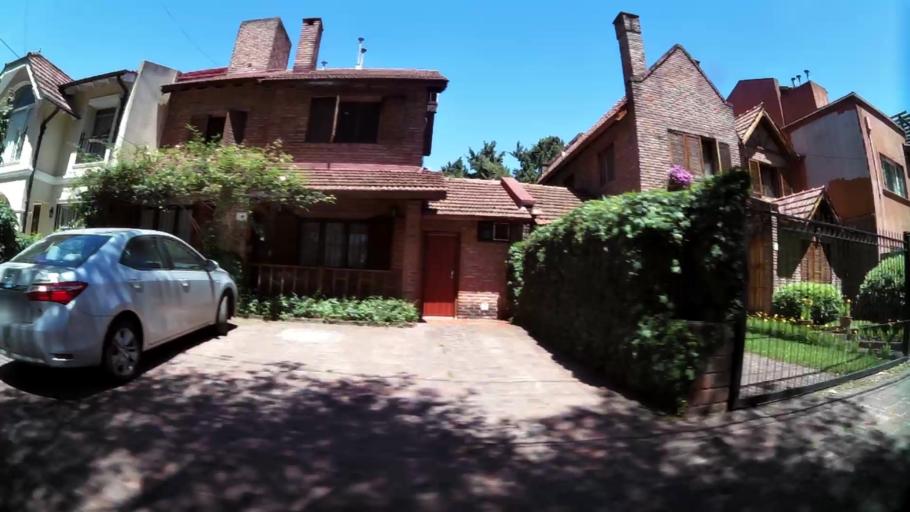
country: AR
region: Buenos Aires
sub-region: Partido de San Isidro
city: San Isidro
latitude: -34.4576
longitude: -58.5084
